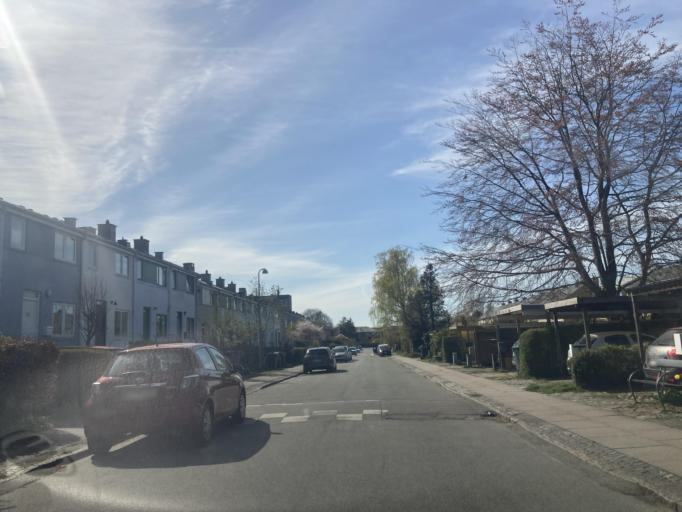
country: DK
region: Capital Region
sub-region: Gladsaxe Municipality
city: Buddinge
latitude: 55.7613
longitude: 12.4645
